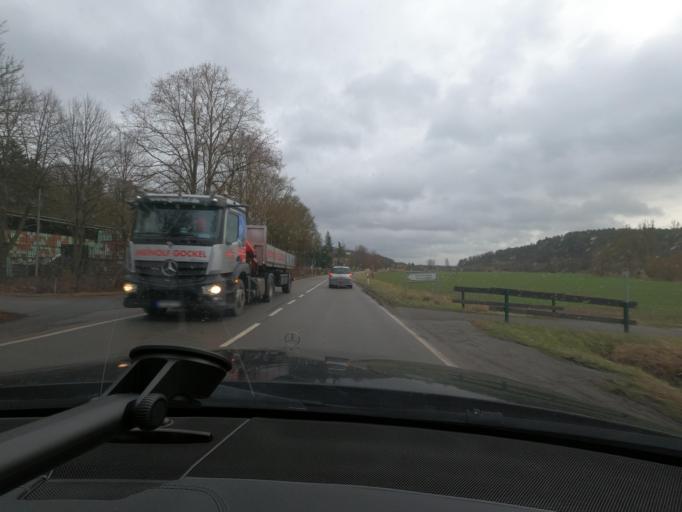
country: DE
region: Hesse
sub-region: Regierungsbezirk Kassel
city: Volkmarsen
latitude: 51.4073
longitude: 9.1362
